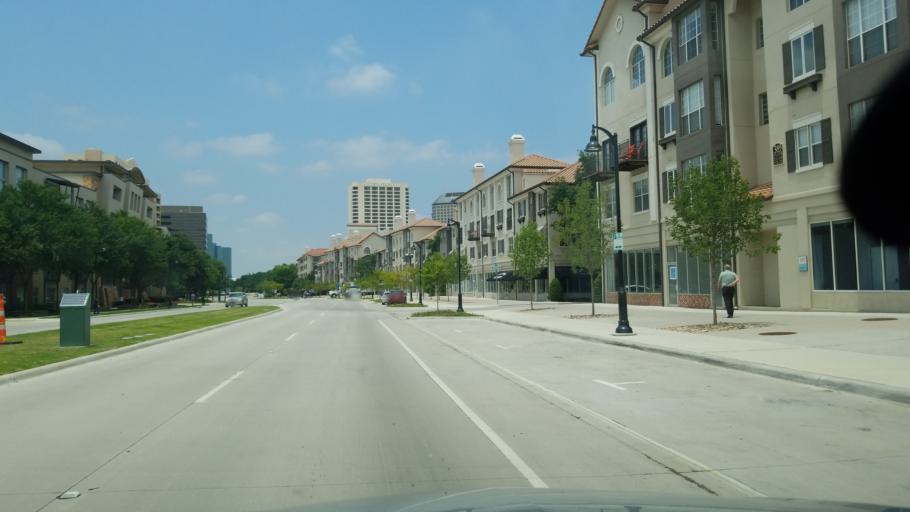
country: US
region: Texas
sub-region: Dallas County
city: Irving
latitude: 32.8634
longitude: -96.9354
